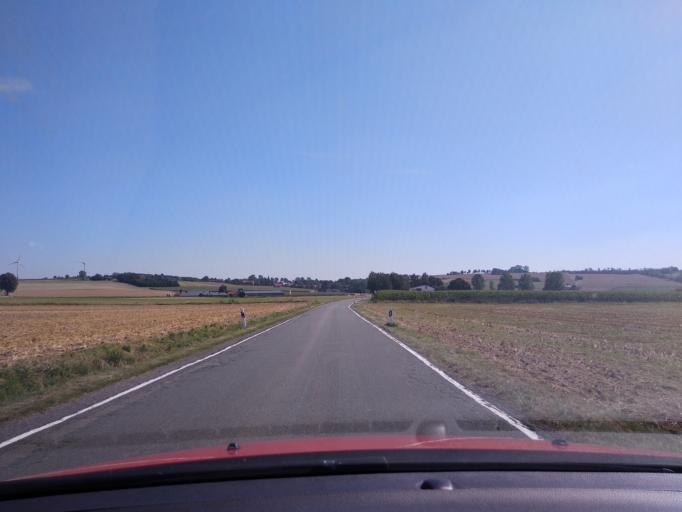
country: DE
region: North Rhine-Westphalia
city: Brakel
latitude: 51.6486
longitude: 9.1706
